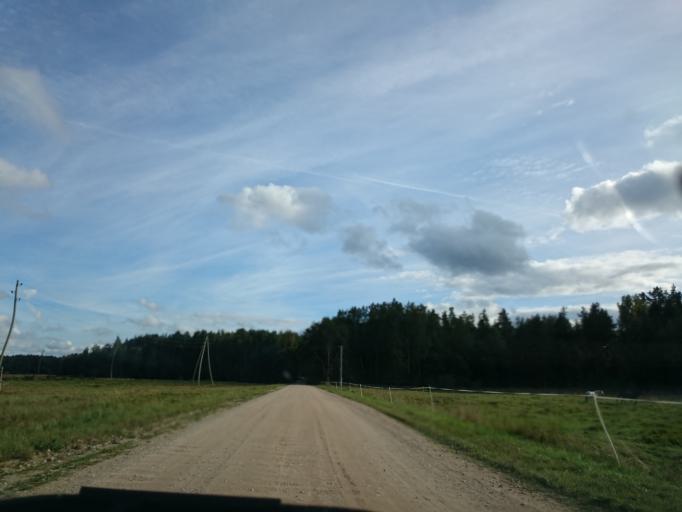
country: LV
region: Adazi
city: Adazi
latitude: 57.0640
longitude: 24.3635
